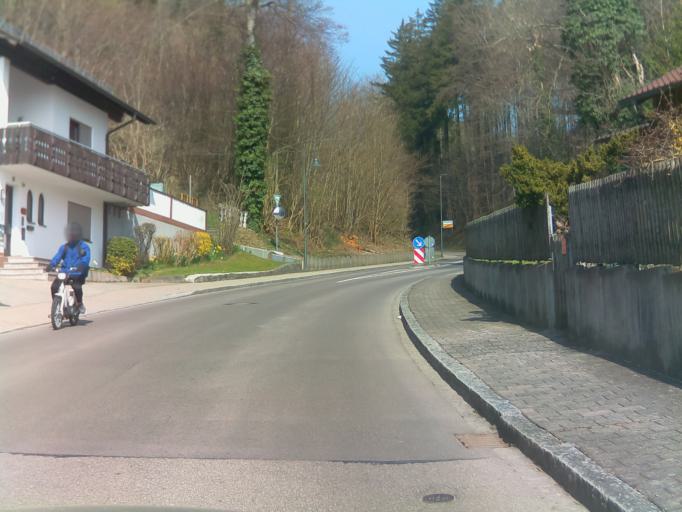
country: DE
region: Bavaria
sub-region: Swabia
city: Altenstadt
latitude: 48.1601
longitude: 10.1179
